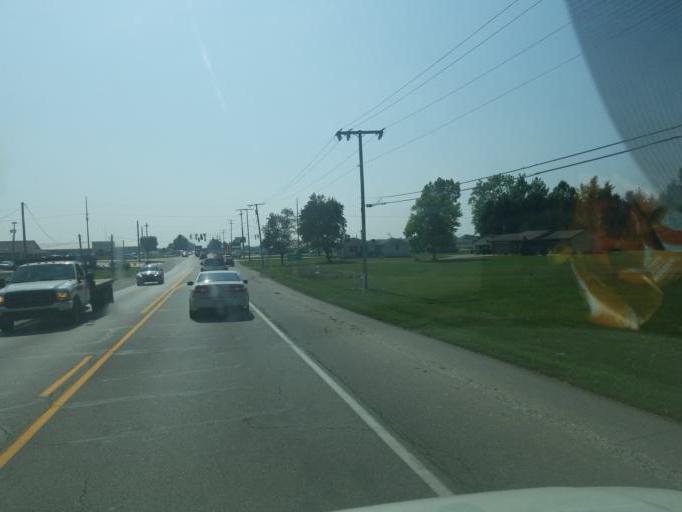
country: US
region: Indiana
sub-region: LaGrange County
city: Topeka
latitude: 41.6562
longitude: -85.5803
